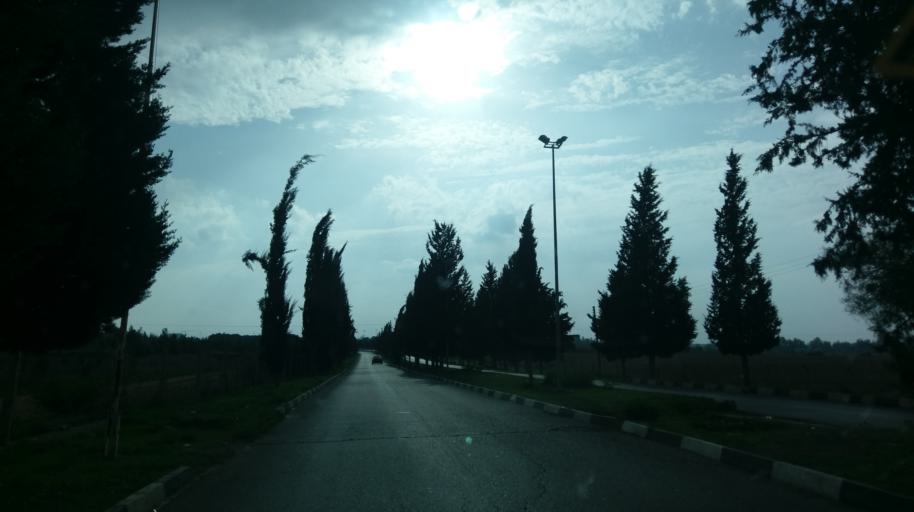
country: CY
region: Lefkosia
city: Nicosia
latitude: 35.1877
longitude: 33.3250
